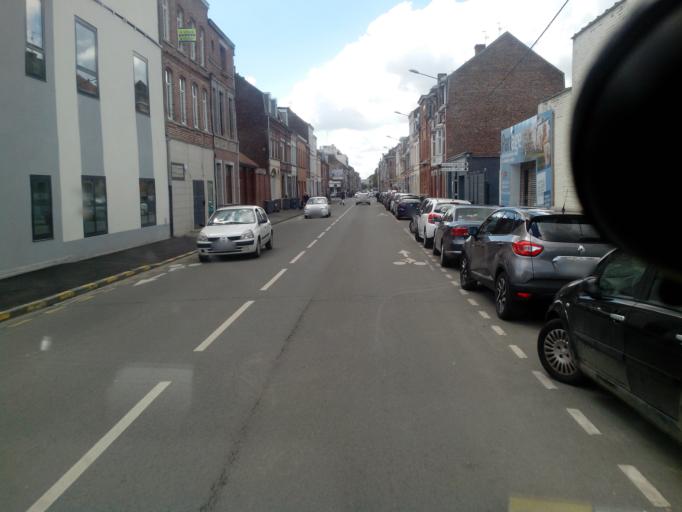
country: FR
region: Nord-Pas-de-Calais
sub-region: Departement du Nord
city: Armentieres
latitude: 50.6889
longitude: 2.8779
